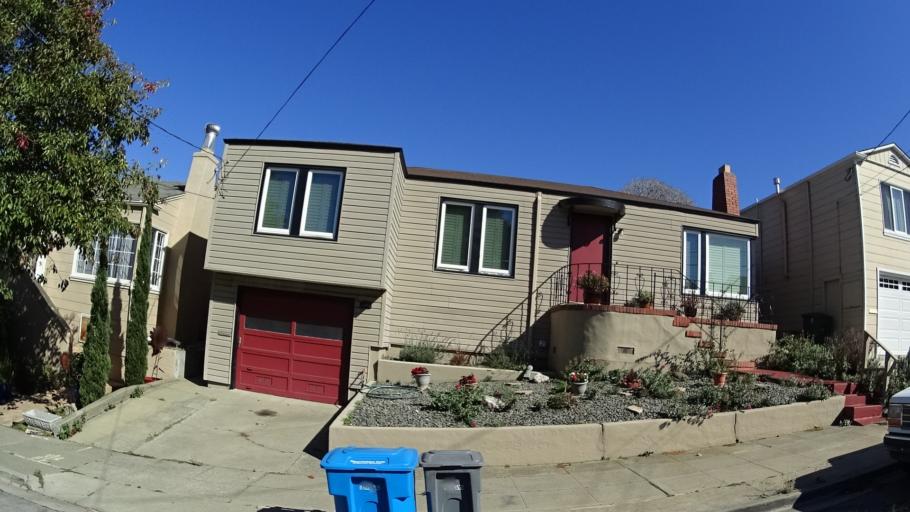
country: US
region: California
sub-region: San Mateo County
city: San Bruno
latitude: 37.6174
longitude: -122.4197
